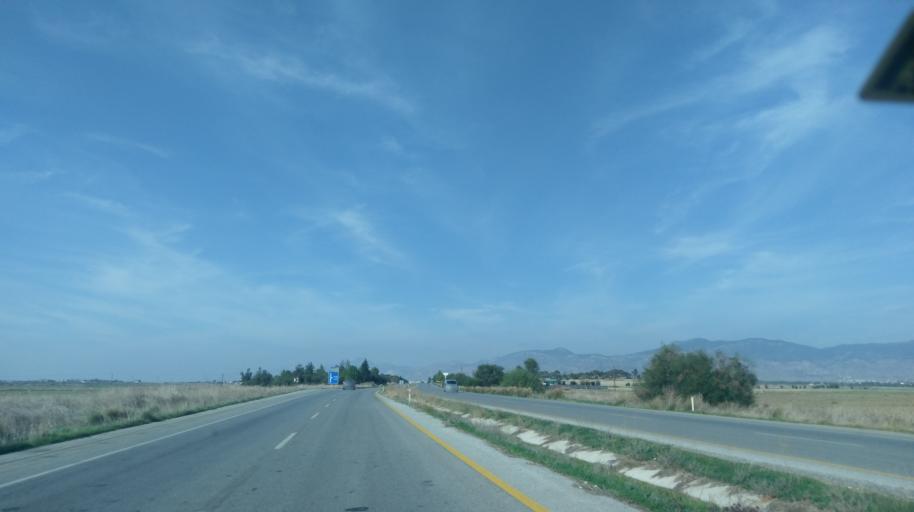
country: CY
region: Ammochostos
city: Lefkonoiko
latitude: 35.1920
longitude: 33.6239
